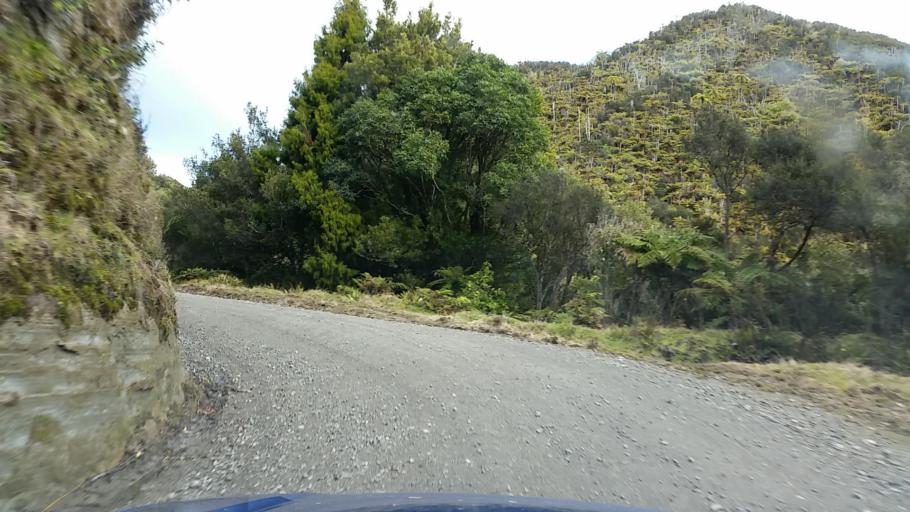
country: NZ
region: Taranaki
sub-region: South Taranaki District
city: Eltham
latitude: -39.2740
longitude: 174.7454
